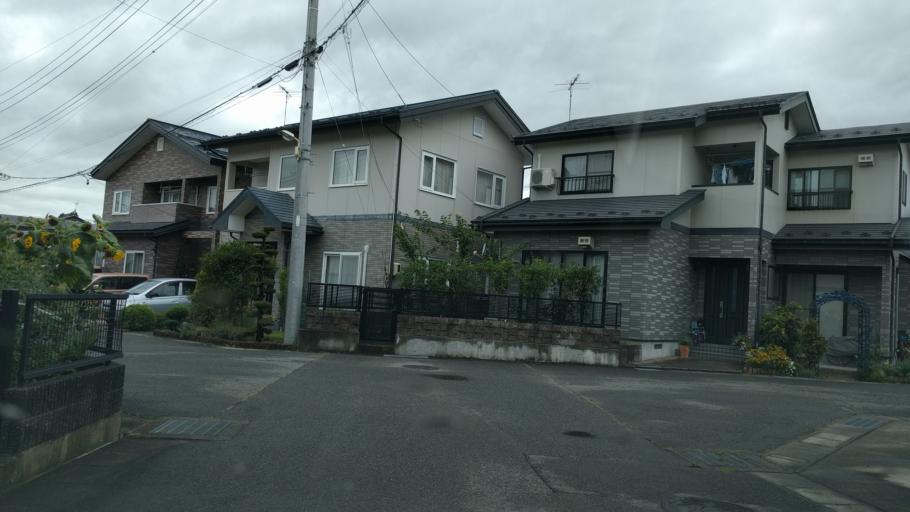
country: JP
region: Fukushima
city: Kitakata
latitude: 37.5065
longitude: 139.9494
